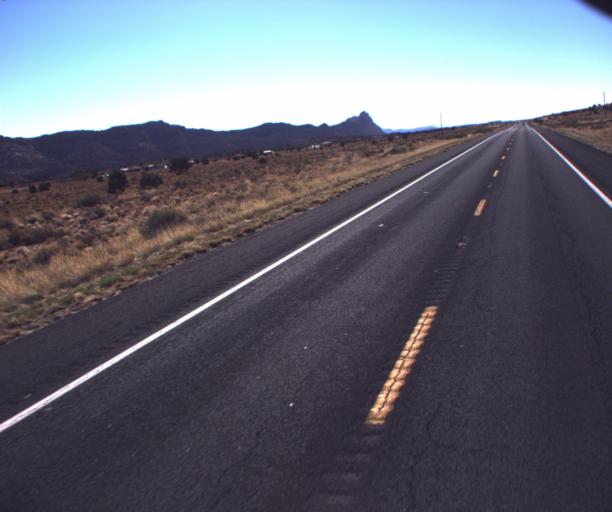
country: US
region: Arizona
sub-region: Coconino County
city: Tuba City
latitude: 36.3780
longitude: -111.5178
